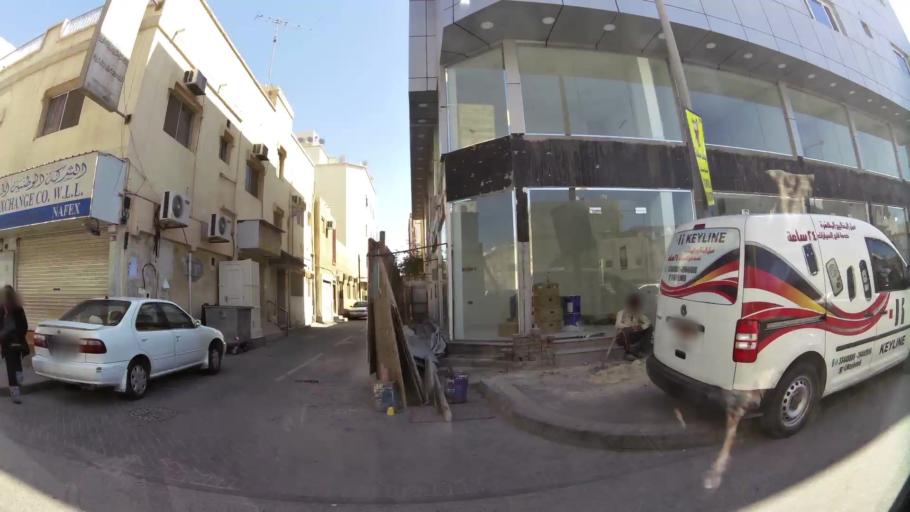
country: BH
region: Muharraq
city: Al Muharraq
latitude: 26.2575
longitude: 50.6169
